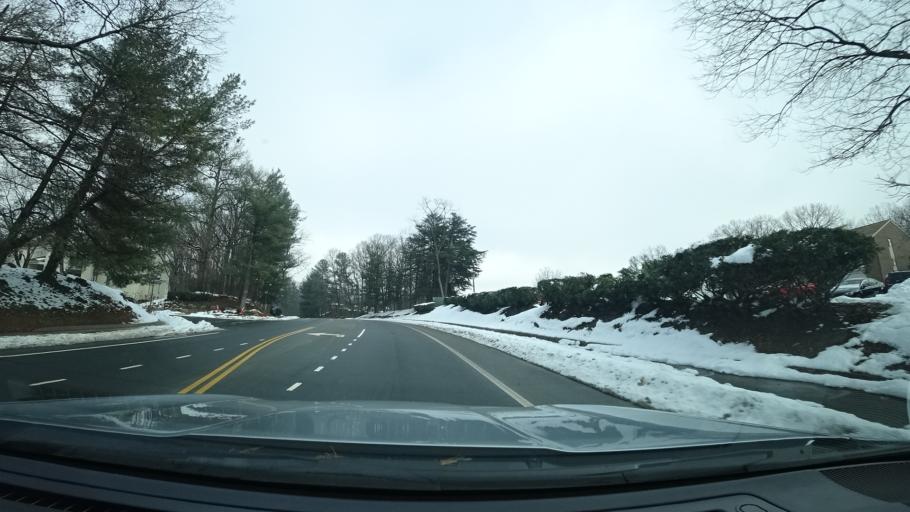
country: US
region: Virginia
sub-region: Fairfax County
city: Reston
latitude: 38.9392
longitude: -77.3608
